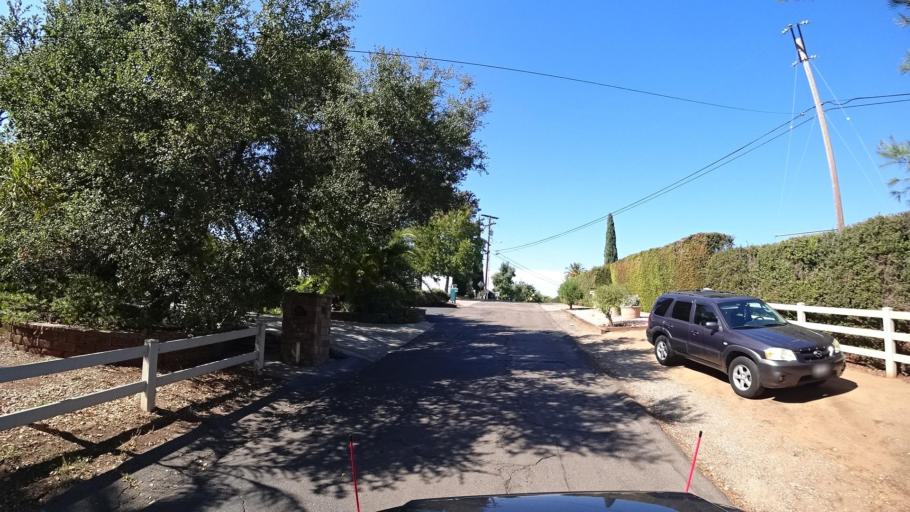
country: US
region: California
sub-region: San Diego County
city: Rancho San Diego
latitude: 32.7740
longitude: -116.9350
